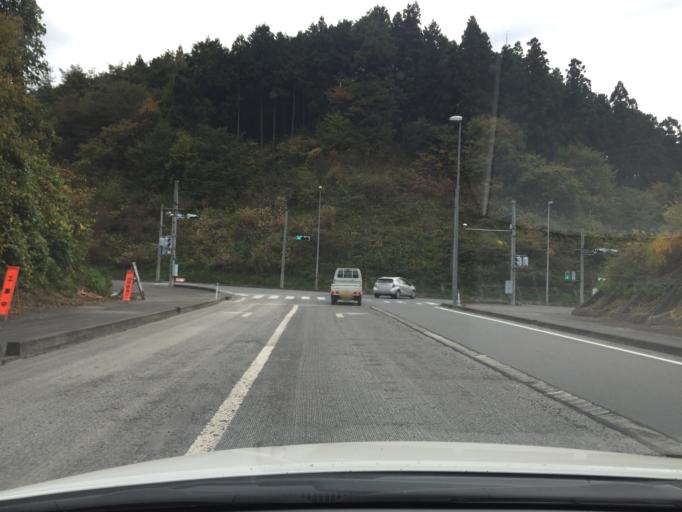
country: JP
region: Fukushima
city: Ishikawa
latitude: 37.0437
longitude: 140.3751
